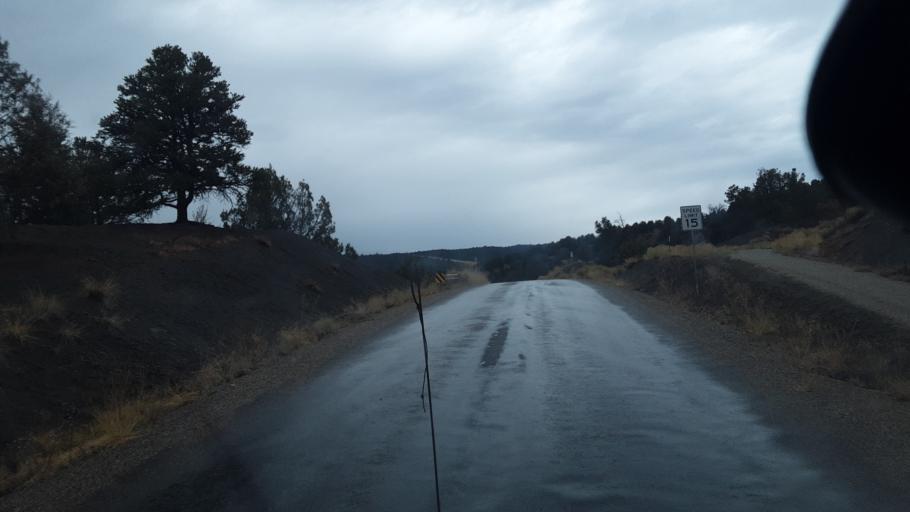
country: US
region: Colorado
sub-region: La Plata County
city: Durango
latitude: 37.2308
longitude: -107.9055
